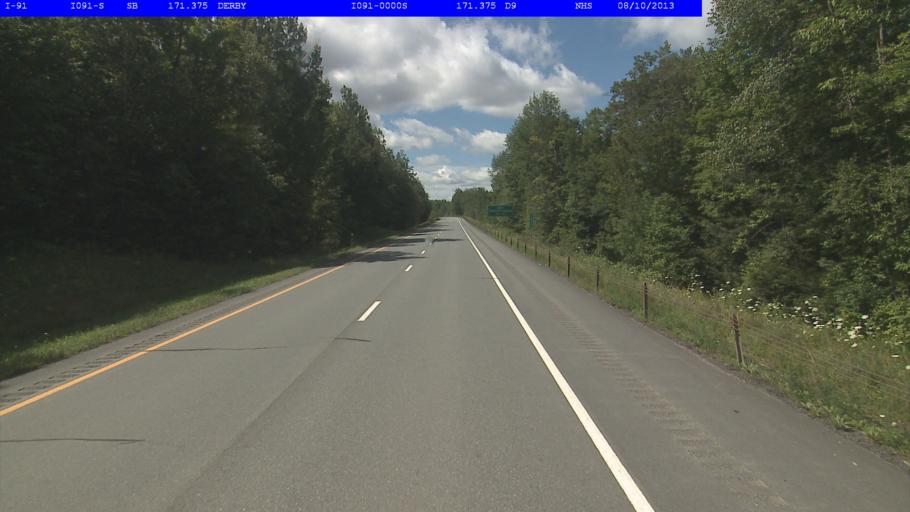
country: US
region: Vermont
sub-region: Orleans County
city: Newport
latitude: 44.9397
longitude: -72.1616
